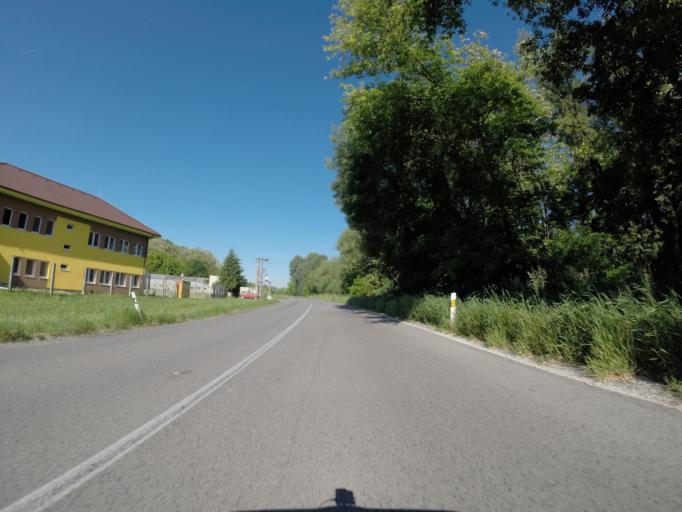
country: SK
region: Nitriansky
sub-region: Okres Nitra
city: Nitra
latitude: 48.5327
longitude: 18.1263
